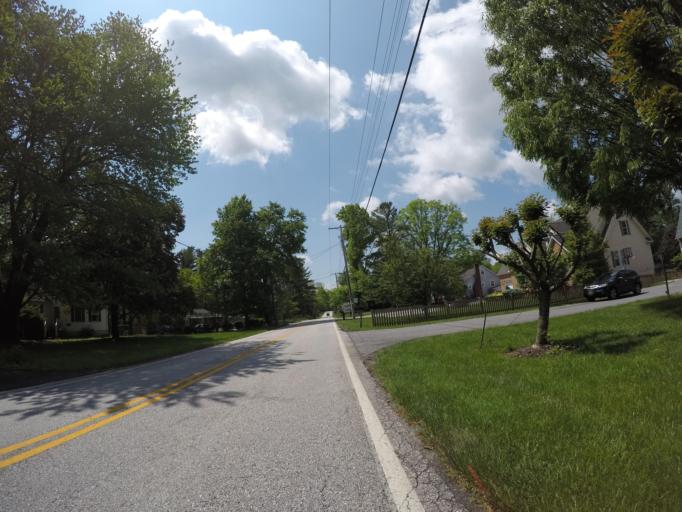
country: US
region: Maryland
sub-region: Howard County
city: Columbia
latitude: 39.2920
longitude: -76.8568
